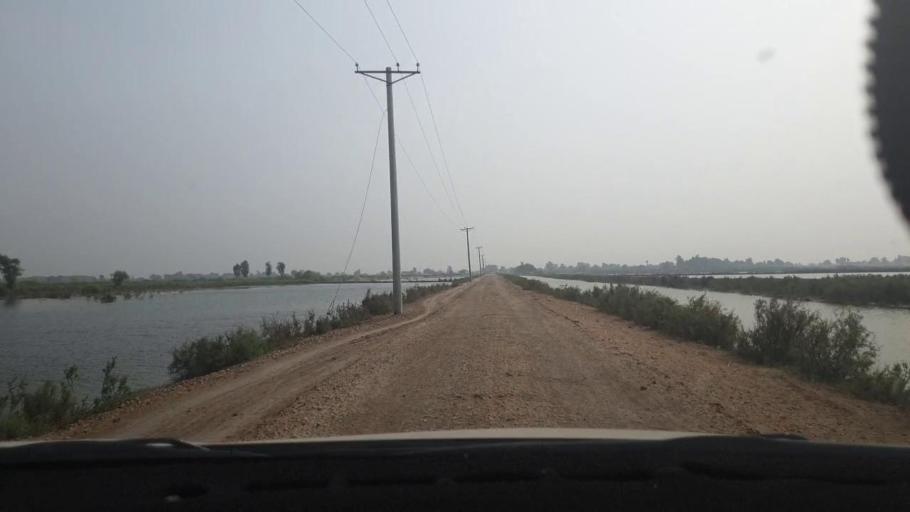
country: PK
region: Sindh
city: Tando Muhammad Khan
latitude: 25.0787
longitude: 68.4942
